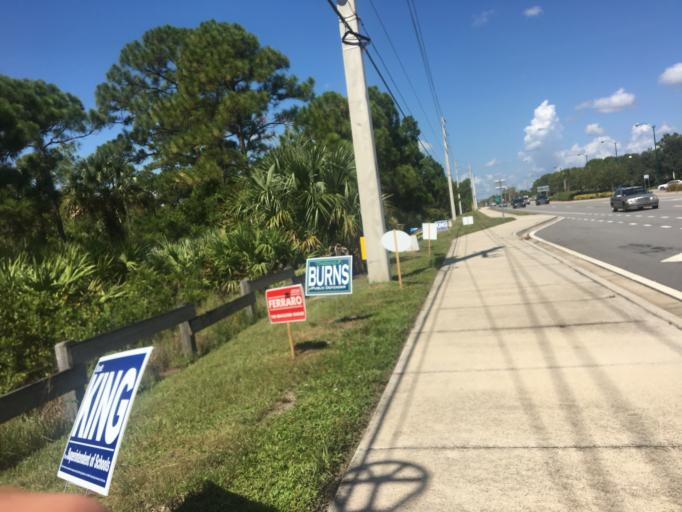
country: US
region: Florida
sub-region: Martin County
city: Palm City
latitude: 27.1610
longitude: -80.2701
